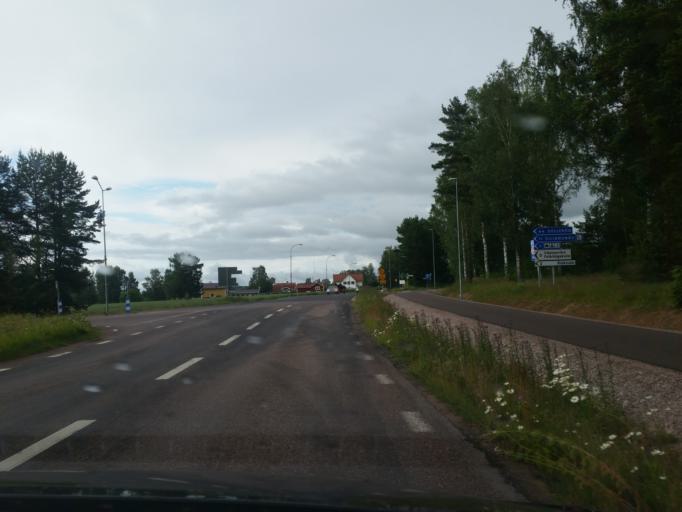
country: SE
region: Dalarna
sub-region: Leksand Municipality
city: Leksand
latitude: 60.7156
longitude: 14.9879
